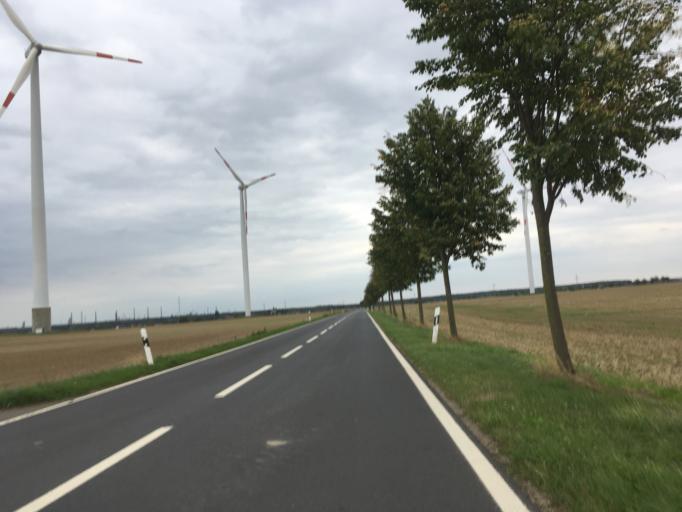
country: DE
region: Brandenburg
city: Meyenburg
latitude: 53.0902
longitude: 14.1787
